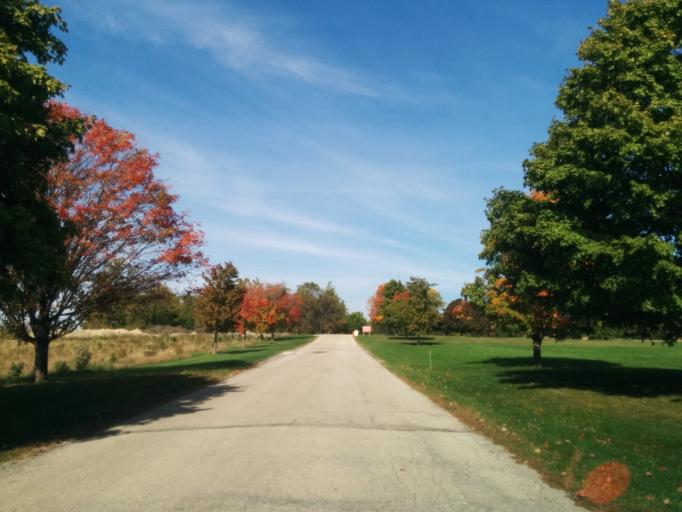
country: US
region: Illinois
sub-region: Kane County
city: North Aurora
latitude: 41.8117
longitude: -88.2988
